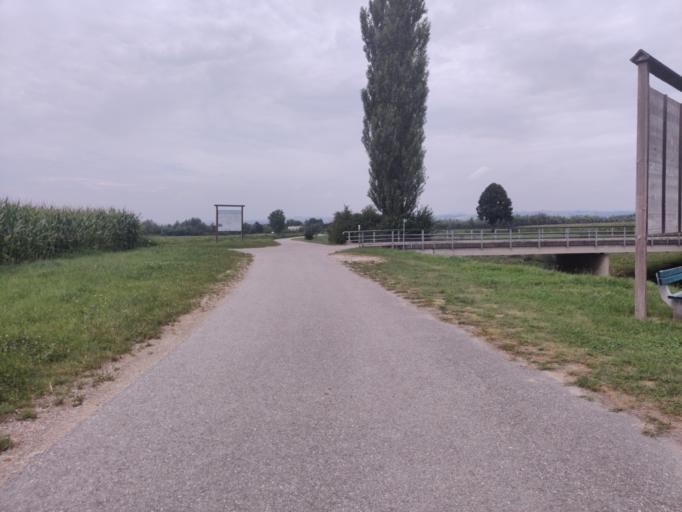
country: AT
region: Lower Austria
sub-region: Politischer Bezirk Amstetten
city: Strengberg
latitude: 48.1846
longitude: 14.7196
